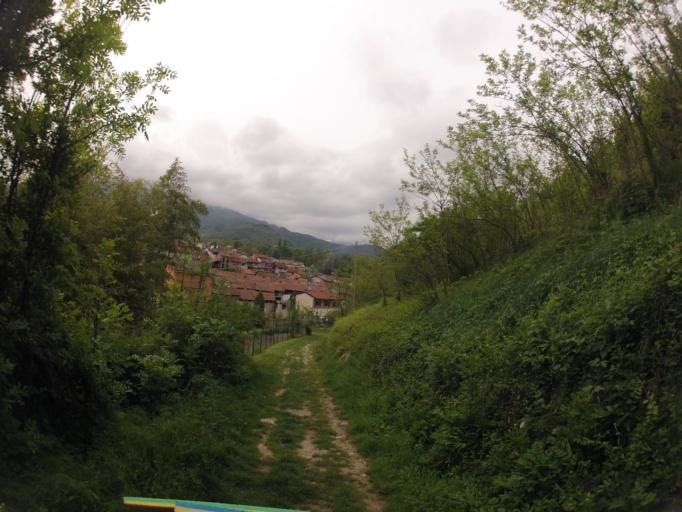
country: IT
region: Piedmont
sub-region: Provincia di Cuneo
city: Peveragno
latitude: 44.3319
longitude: 7.6144
